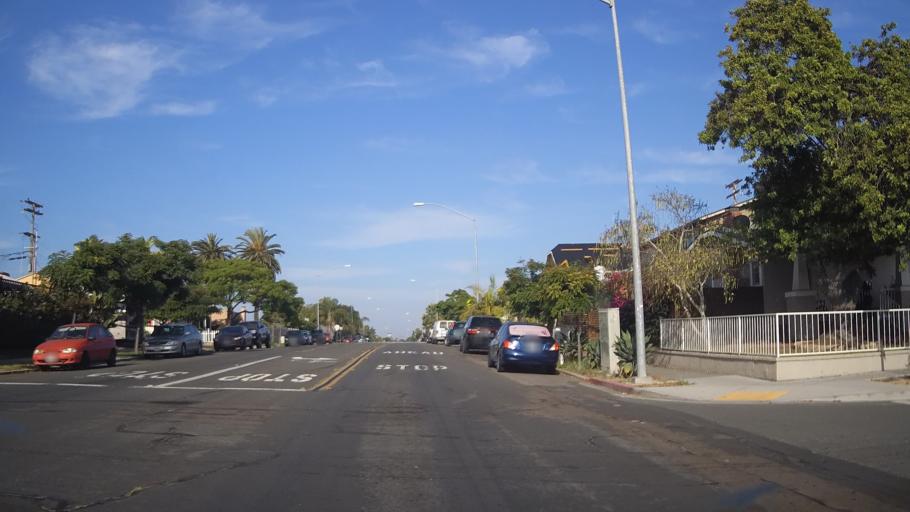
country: US
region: California
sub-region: San Diego County
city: San Diego
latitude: 32.7573
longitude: -117.1364
